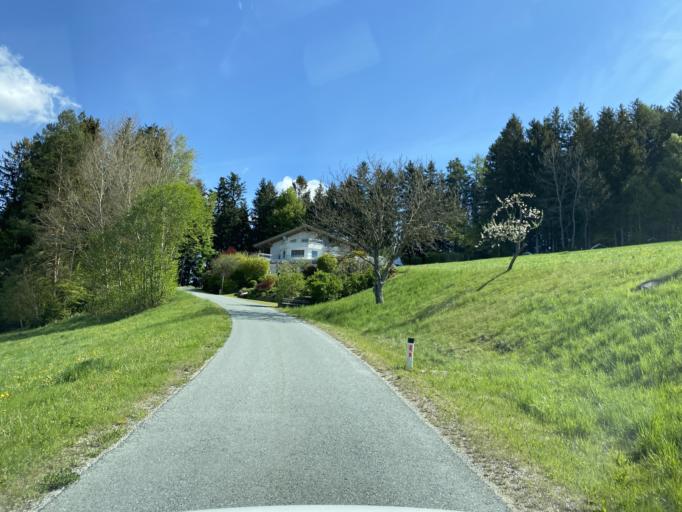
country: AT
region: Styria
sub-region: Politischer Bezirk Weiz
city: Birkfeld
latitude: 47.3688
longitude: 15.6977
